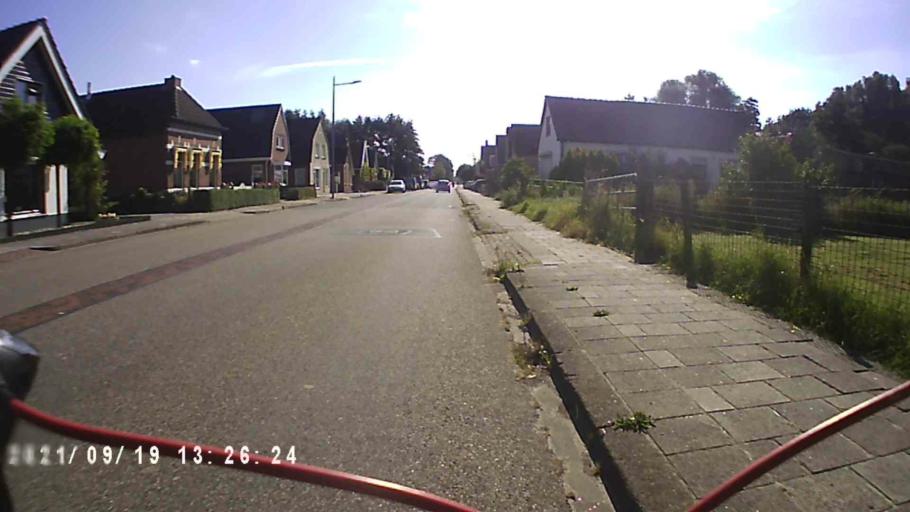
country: NL
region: Groningen
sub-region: Gemeente  Oldambt
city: Winschoten
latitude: 53.1536
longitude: 7.0165
